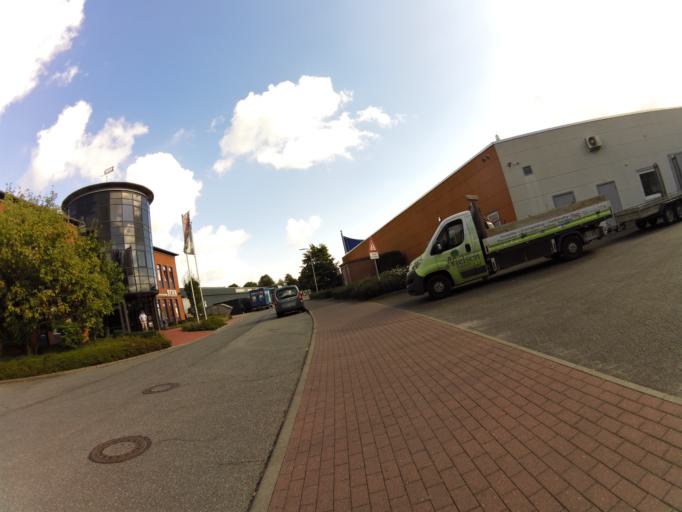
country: DE
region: Schleswig-Holstein
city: Eckernforde
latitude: 54.4512
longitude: 9.8290
